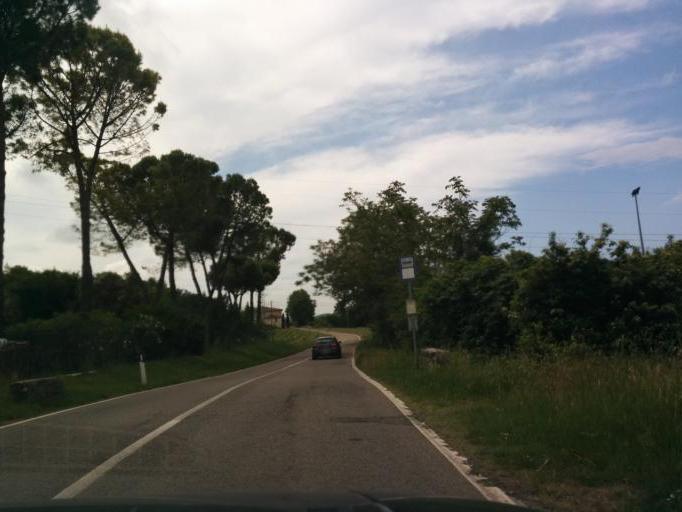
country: IT
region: Tuscany
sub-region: Province of Florence
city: Sambuca
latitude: 43.6051
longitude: 11.1947
